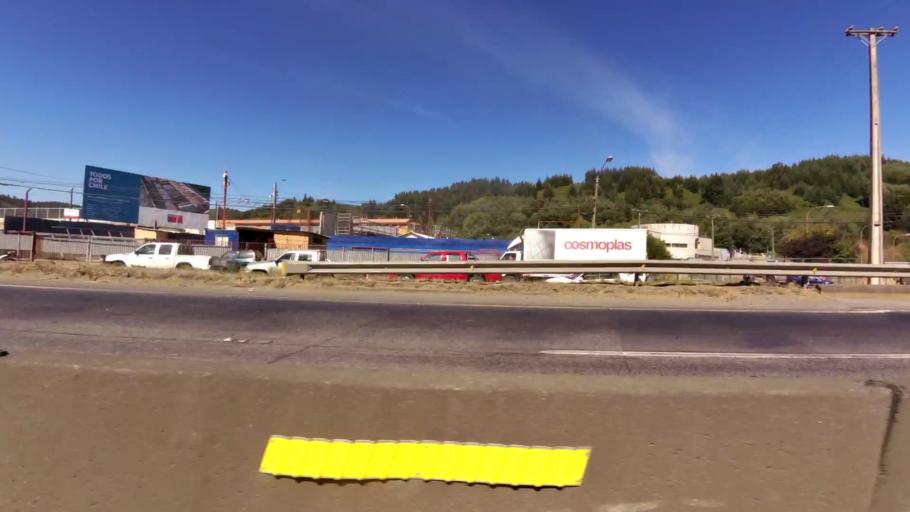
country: CL
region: Biobio
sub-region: Provincia de Concepcion
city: Concepcion
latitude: -36.8068
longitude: -73.0241
